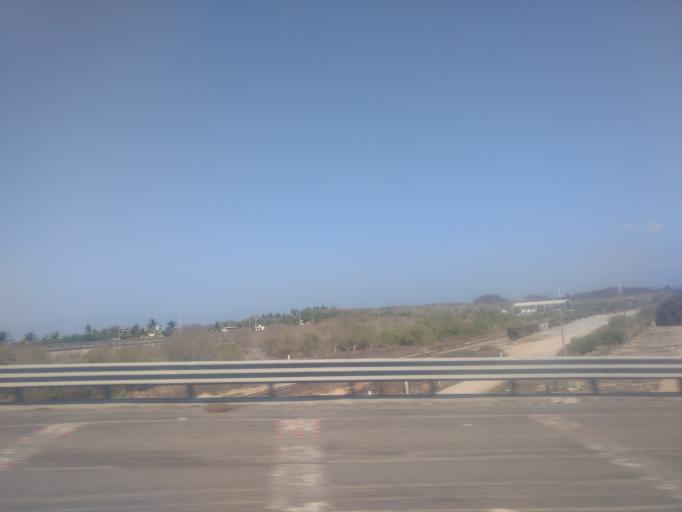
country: MX
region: Colima
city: El Colomo
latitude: 18.9980
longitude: -104.2444
